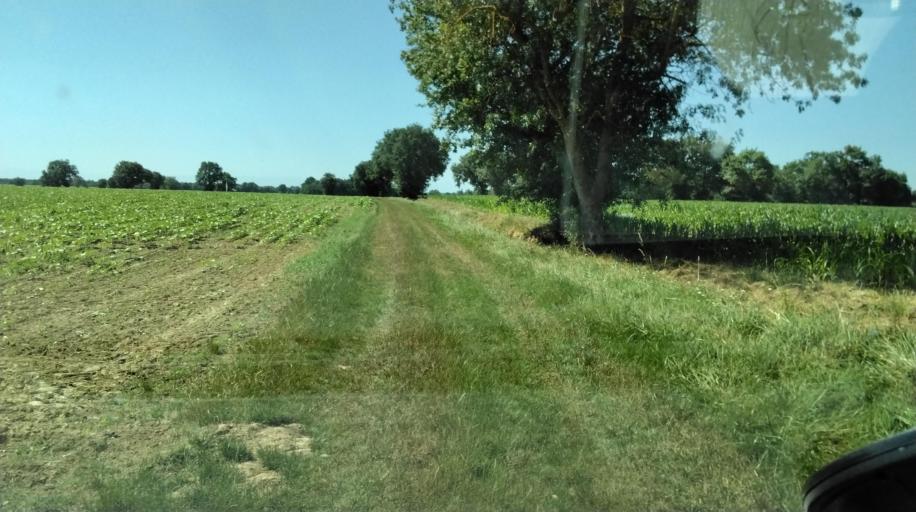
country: FR
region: Midi-Pyrenees
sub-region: Departement de la Haute-Garonne
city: Sainte-Foy-de-Peyrolieres
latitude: 43.4893
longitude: 1.1567
